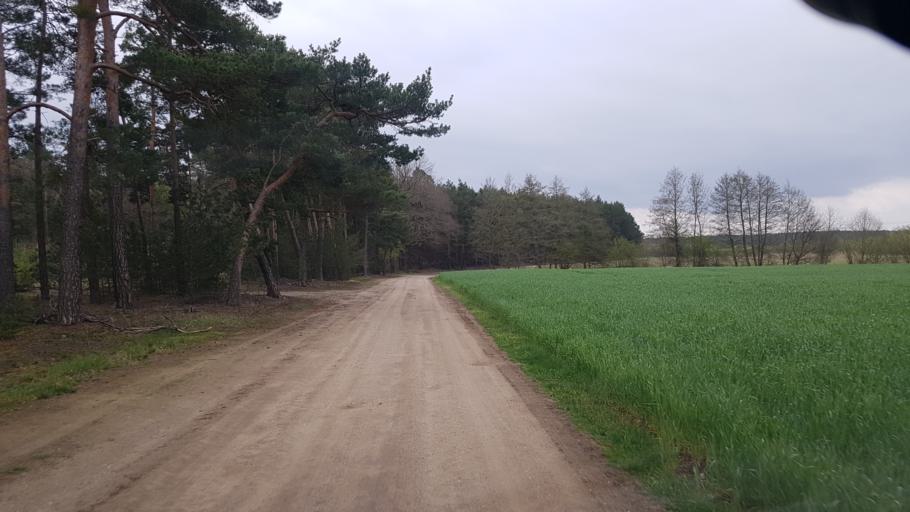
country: DE
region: Brandenburg
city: Altdobern
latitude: 51.6832
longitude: 14.0544
